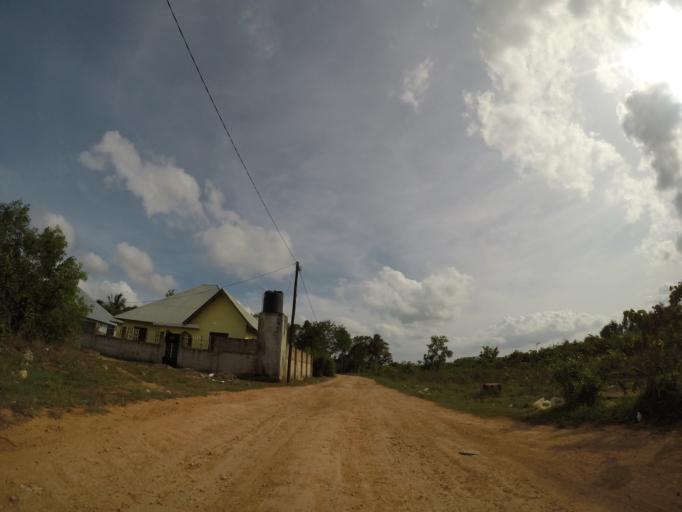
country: TZ
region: Zanzibar Central/South
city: Koani
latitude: -6.2271
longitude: 39.3191
